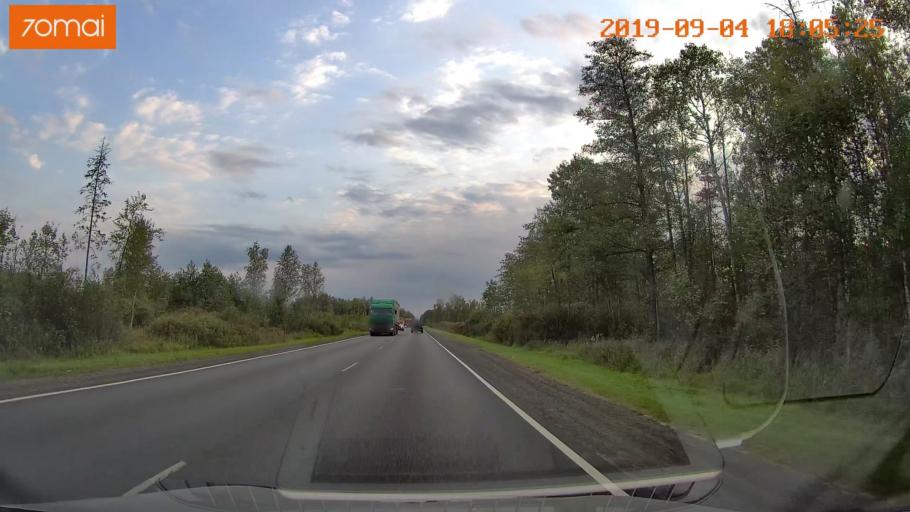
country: RU
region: Moskovskaya
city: Il'inskiy Pogost
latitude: 55.4416
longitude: 38.8268
